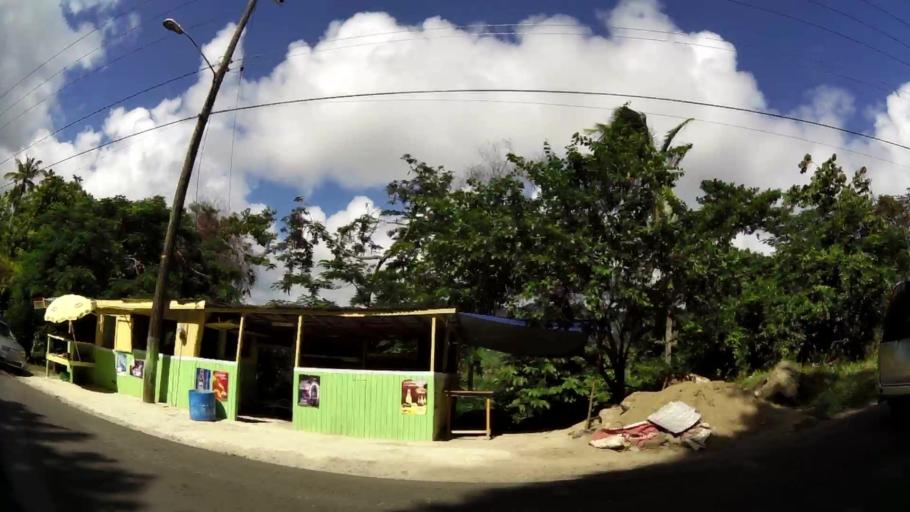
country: LC
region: Dennery Quarter
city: Dennery
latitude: 13.9332
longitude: -60.9096
